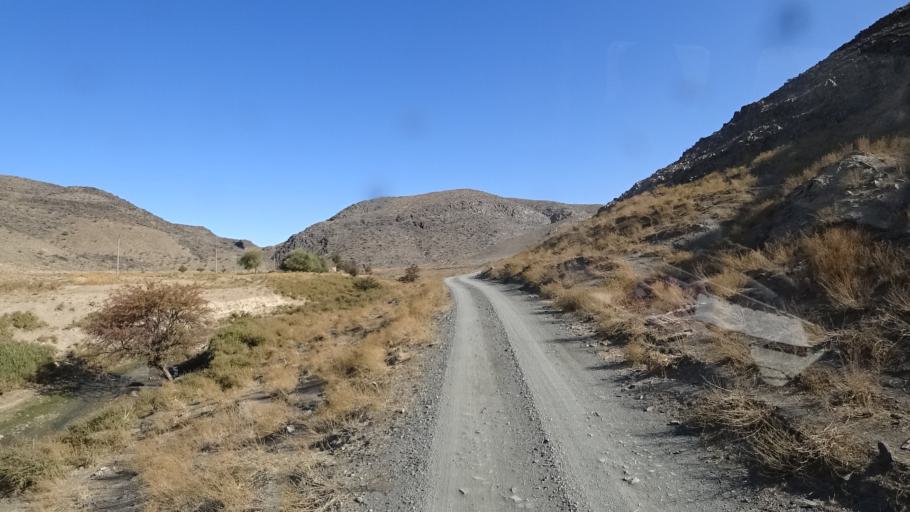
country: UZ
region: Navoiy
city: Nurota
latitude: 40.3003
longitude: 65.6139
